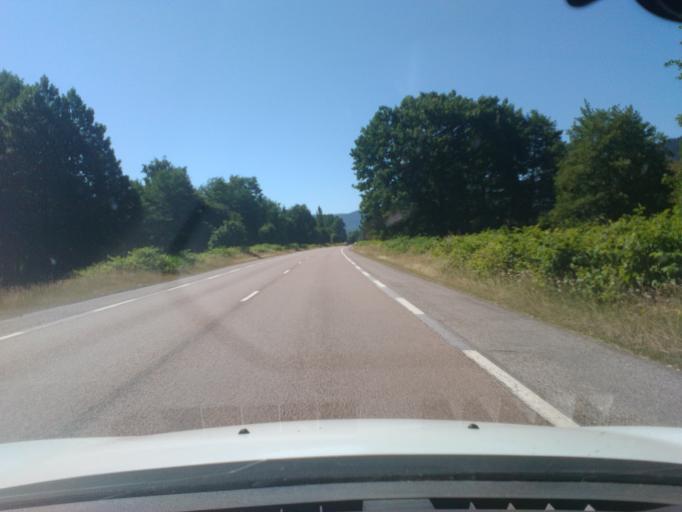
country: FR
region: Lorraine
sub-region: Departement des Vosges
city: Vagney
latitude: 48.0144
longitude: 6.7089
